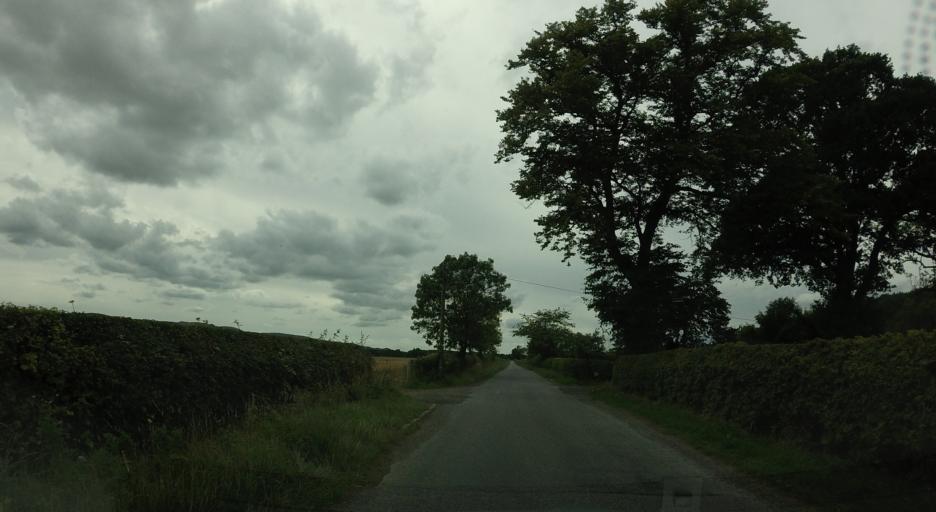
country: GB
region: Scotland
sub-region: Perth and Kinross
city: Bridge of Earn
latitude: 56.3545
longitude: -3.3683
